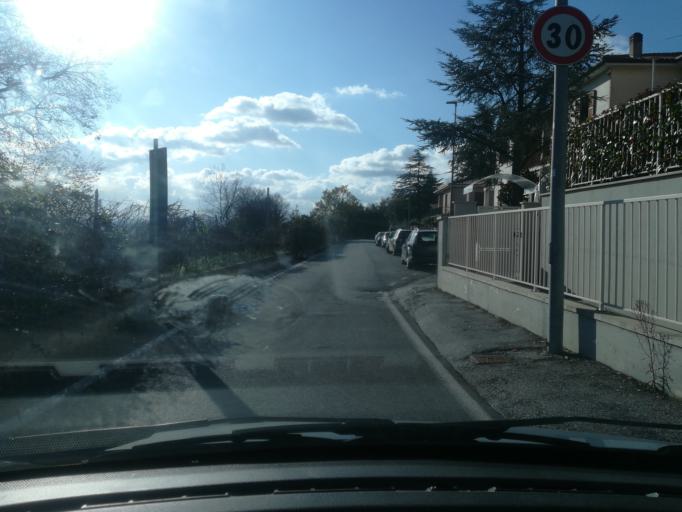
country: IT
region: The Marches
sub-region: Provincia di Macerata
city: Macerata
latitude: 43.2914
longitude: 13.4402
